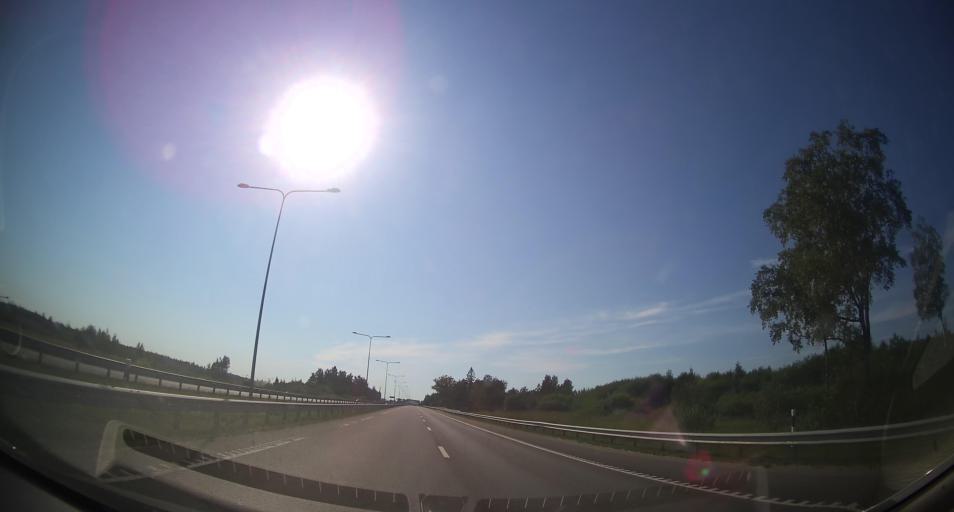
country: EE
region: Harju
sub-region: Maardu linn
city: Maardu
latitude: 59.4522
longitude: 25.0363
